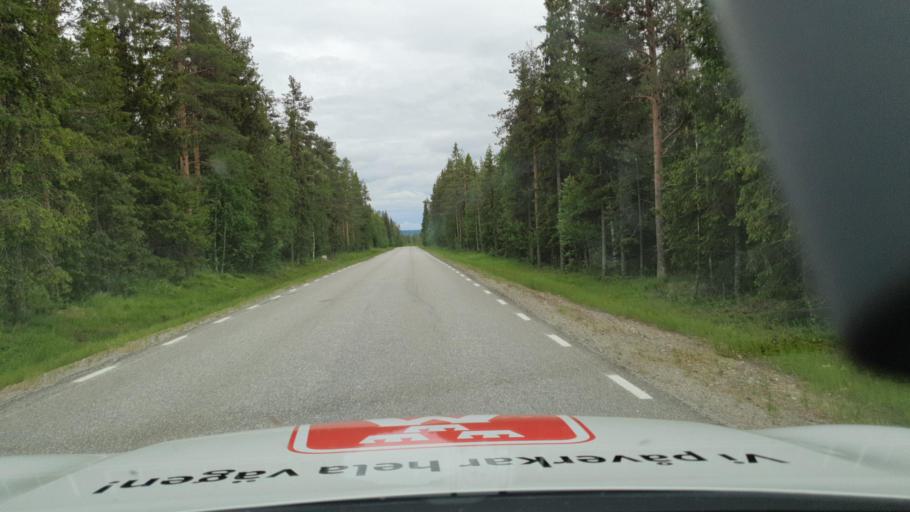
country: SE
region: Vaesterbotten
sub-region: Lycksele Kommun
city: Soderfors
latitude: 64.3112
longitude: 18.1641
